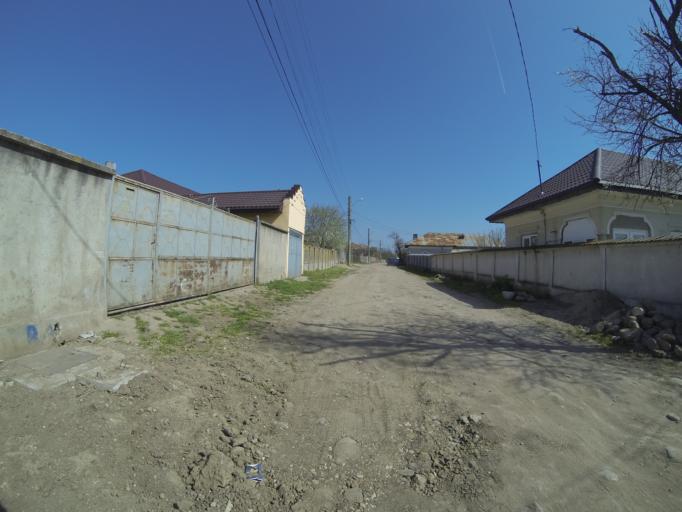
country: RO
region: Dolj
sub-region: Comuna Segarcea
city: Segarcea
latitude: 44.0970
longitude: 23.7354
